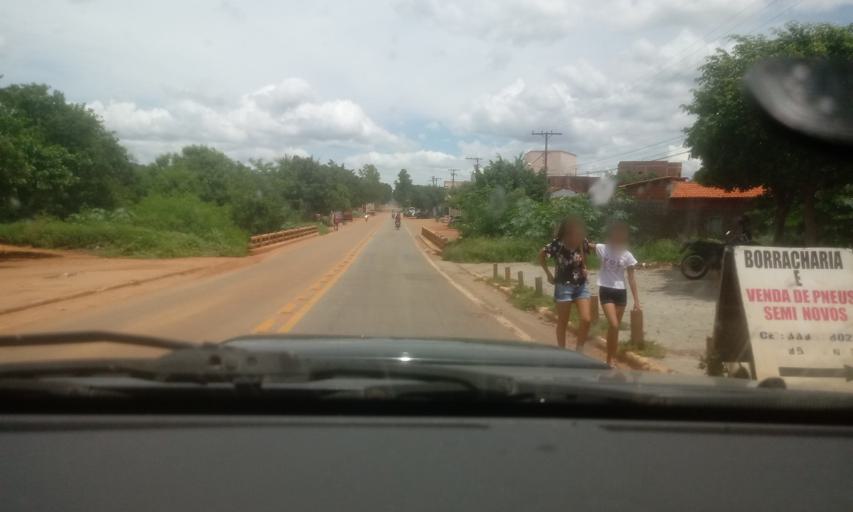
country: BR
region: Bahia
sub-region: Riacho De Santana
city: Riacho de Santana
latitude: -13.6050
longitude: -42.9377
